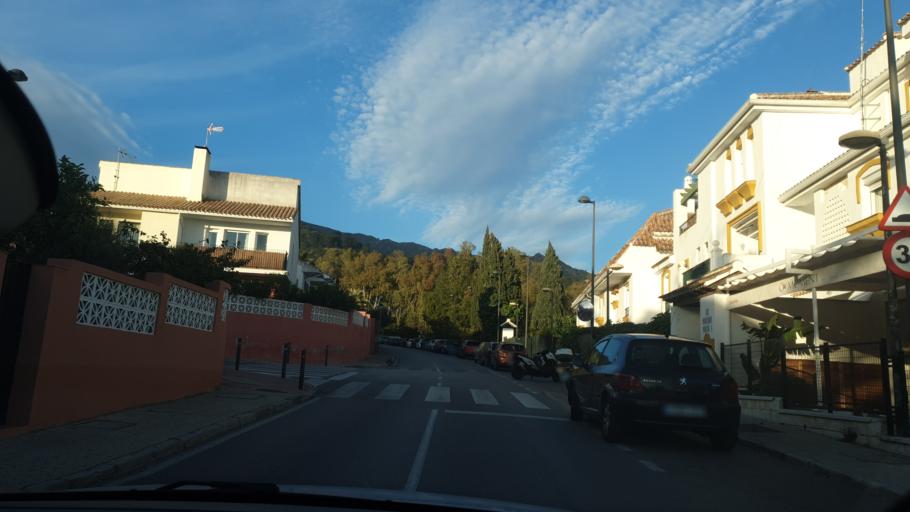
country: ES
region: Andalusia
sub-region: Provincia de Malaga
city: Marbella
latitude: 36.5261
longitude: -4.8950
